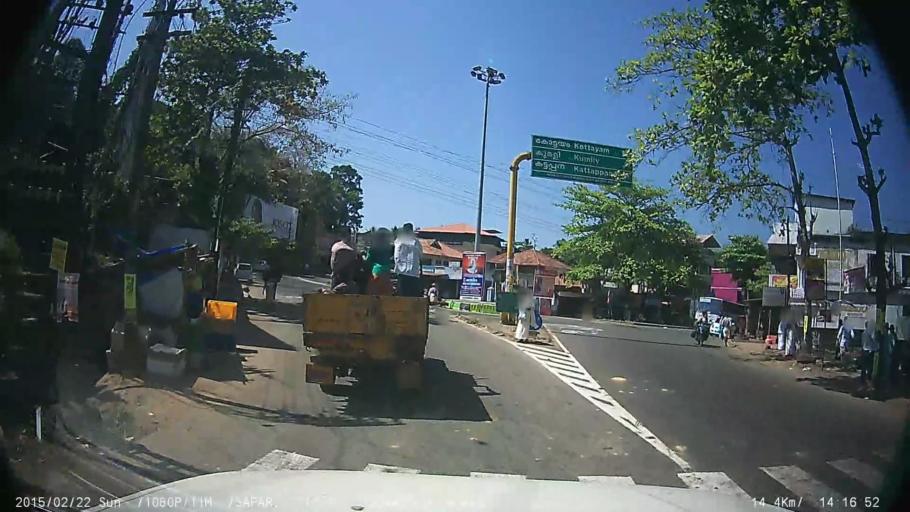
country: IN
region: Kerala
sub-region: Kottayam
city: Lalam
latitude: 9.5590
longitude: 76.6819
